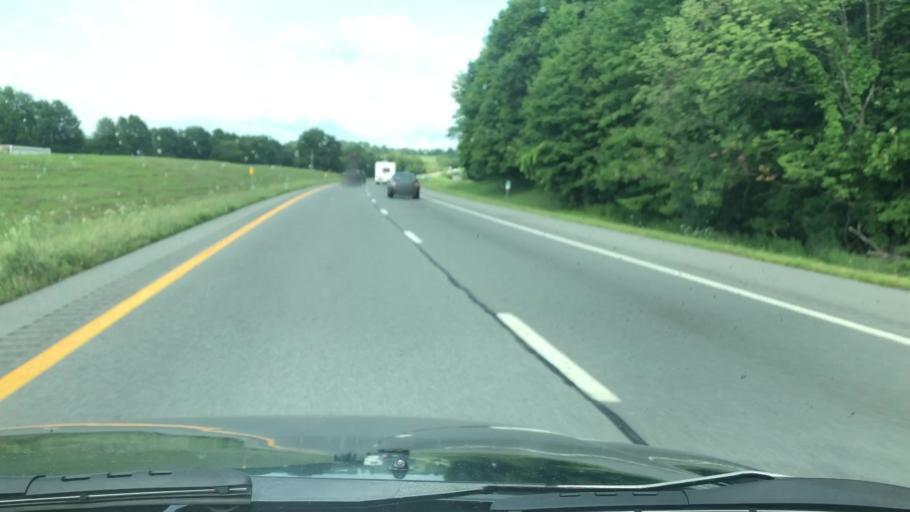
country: US
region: New York
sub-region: Orange County
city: Montgomery
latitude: 41.4963
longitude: -74.2617
